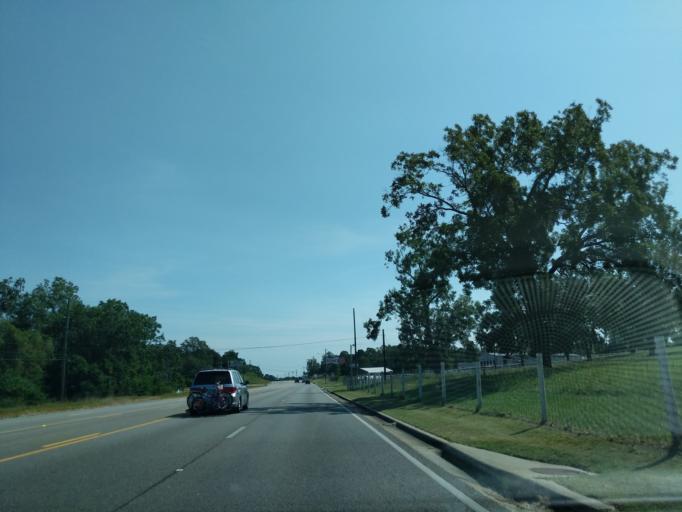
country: US
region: Alabama
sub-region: Covington County
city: Andalusia
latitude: 31.3268
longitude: -86.5106
